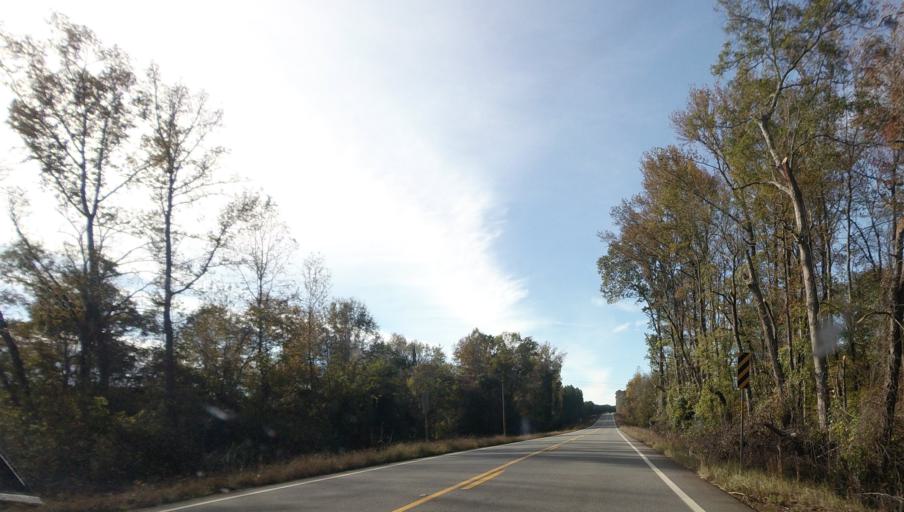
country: US
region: Georgia
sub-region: Taylor County
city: Butler
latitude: 32.7158
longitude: -84.3029
